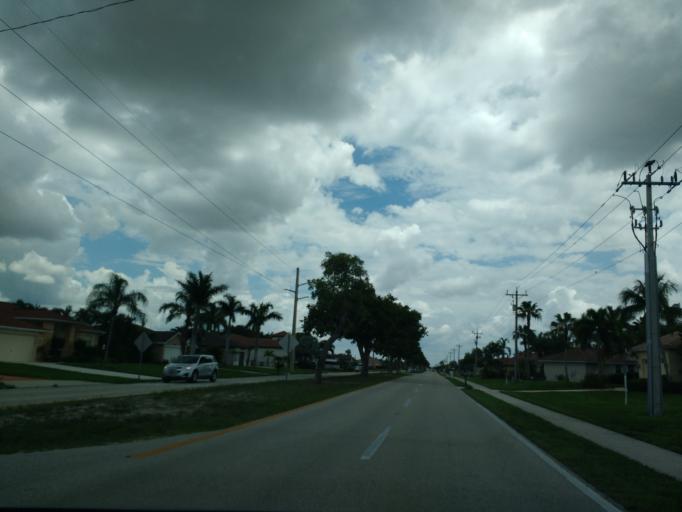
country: US
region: Florida
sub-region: Lee County
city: Cape Coral
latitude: 26.5627
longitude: -82.0162
